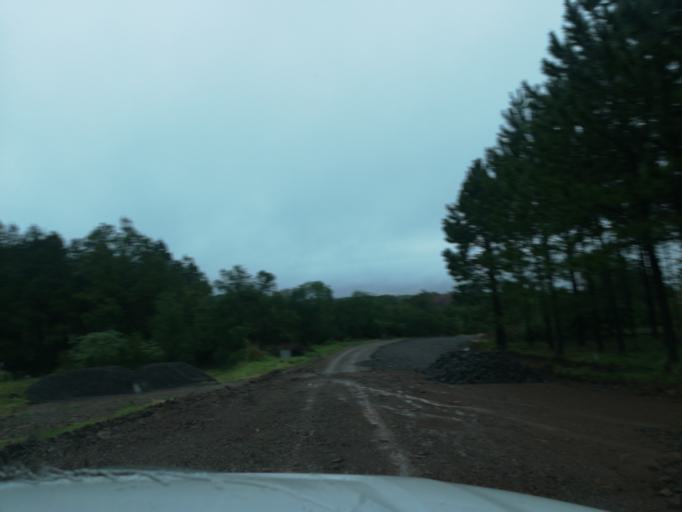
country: AR
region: Misiones
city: Almafuerte
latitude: -27.5384
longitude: -55.4086
